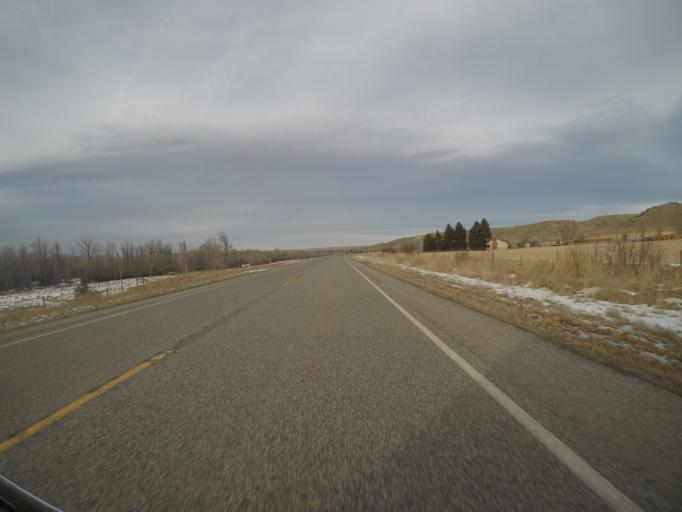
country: US
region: Montana
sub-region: Stillwater County
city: Absarokee
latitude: 45.4700
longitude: -109.4483
